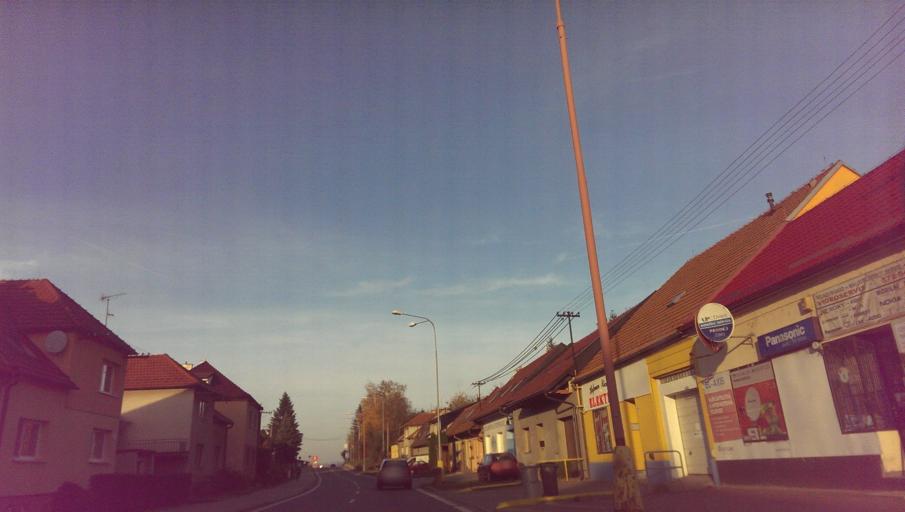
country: CZ
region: Zlin
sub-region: Okres Uherske Hradiste
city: Uherske Hradiste
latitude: 49.0742
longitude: 17.4818
